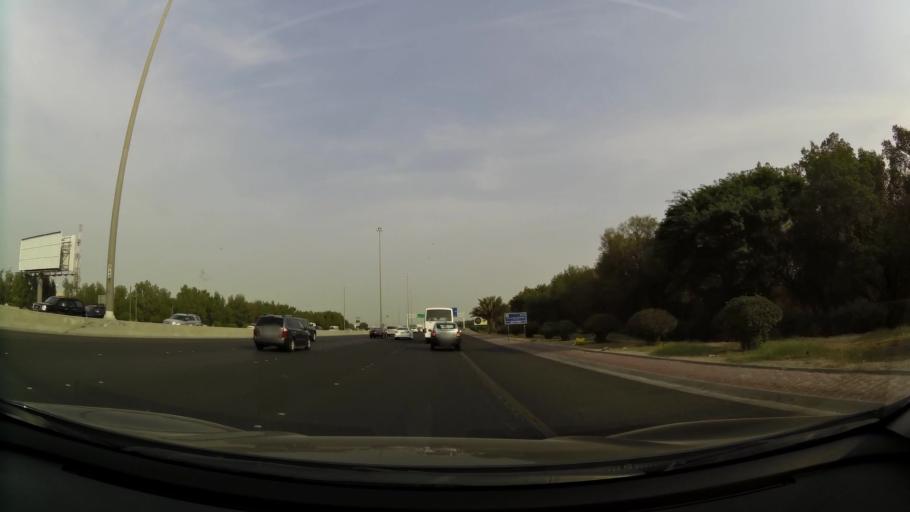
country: KW
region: Al Farwaniyah
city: Janub as Surrah
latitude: 29.2652
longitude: 48.0034
